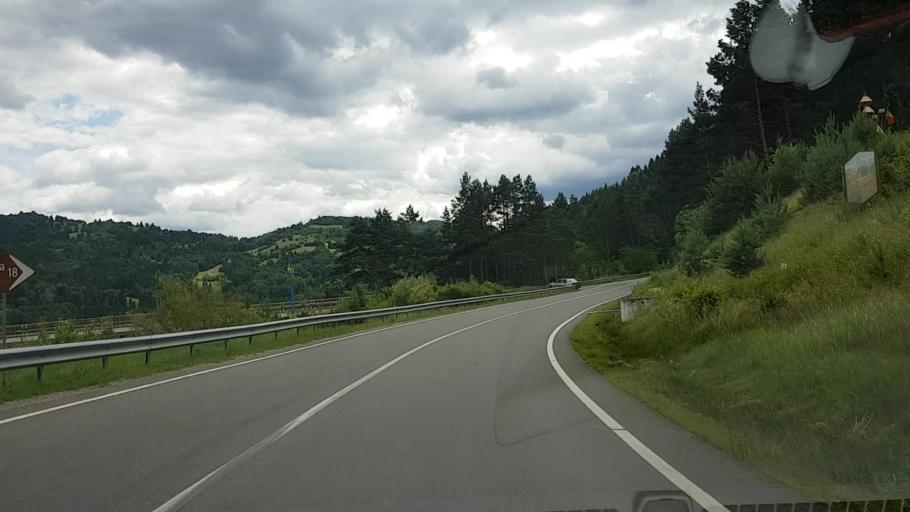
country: RO
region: Neamt
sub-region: Comuna Poiana Teiului
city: Poiana Teiului
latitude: 47.0897
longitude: 25.9597
